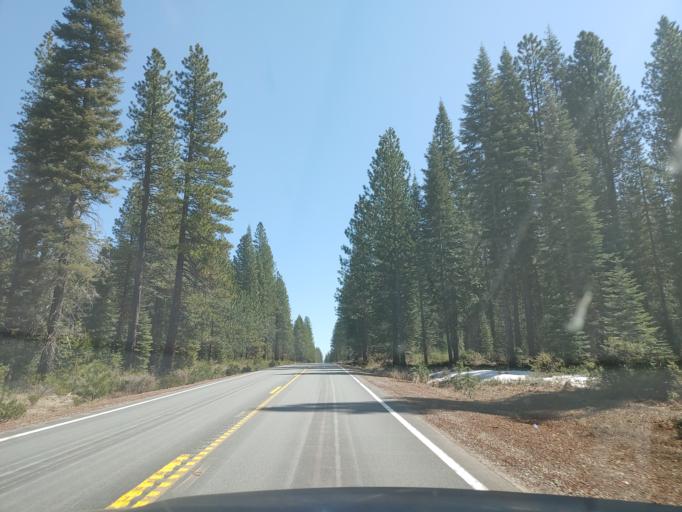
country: US
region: California
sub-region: Siskiyou County
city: McCloud
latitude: 41.2671
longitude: -121.9006
